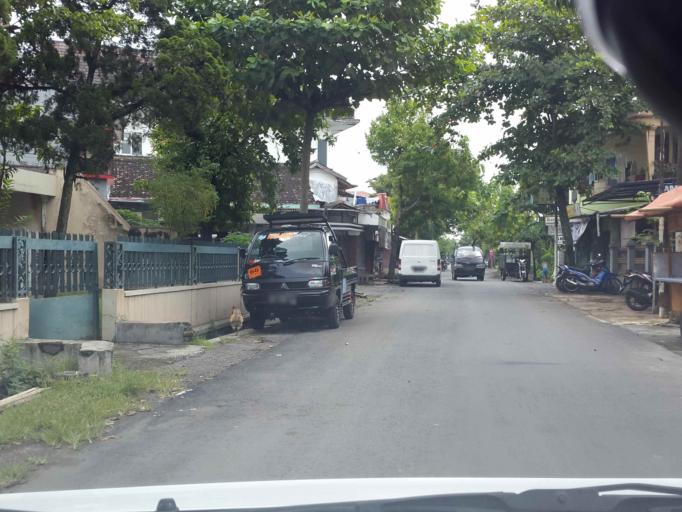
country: ID
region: Central Java
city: Grogol
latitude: -7.5909
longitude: 110.8304
